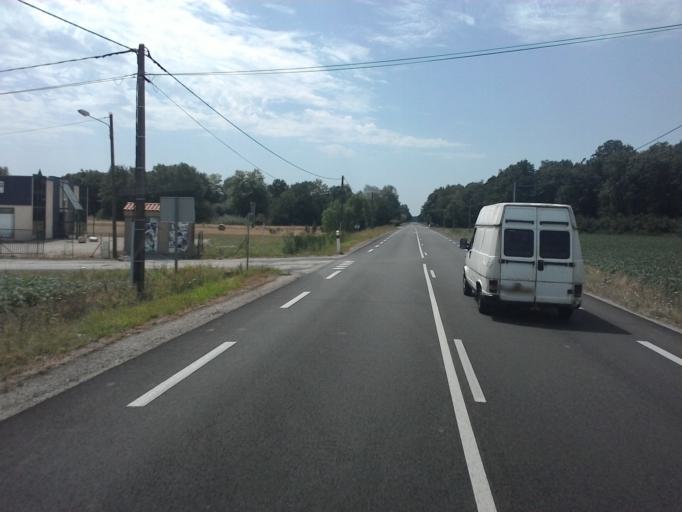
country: FR
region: Rhone-Alpes
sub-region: Departement de l'Ain
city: Saint-Etienne-du-Bois
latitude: 46.2646
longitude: 5.2806
